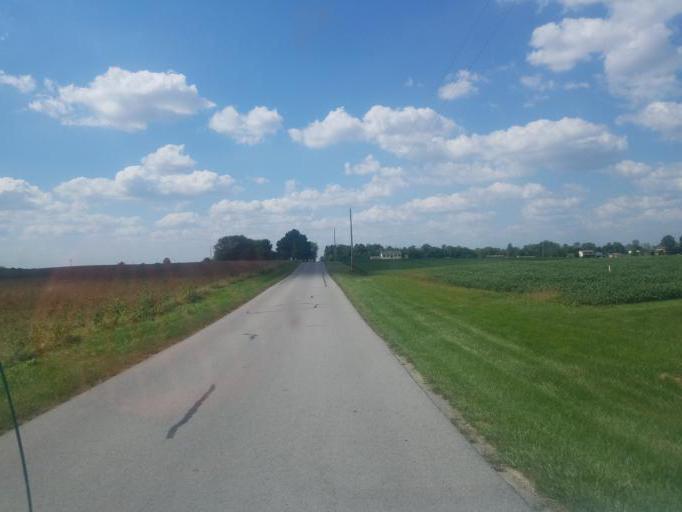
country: US
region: Ohio
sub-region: Allen County
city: Lima
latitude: 40.6515
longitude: -83.9717
